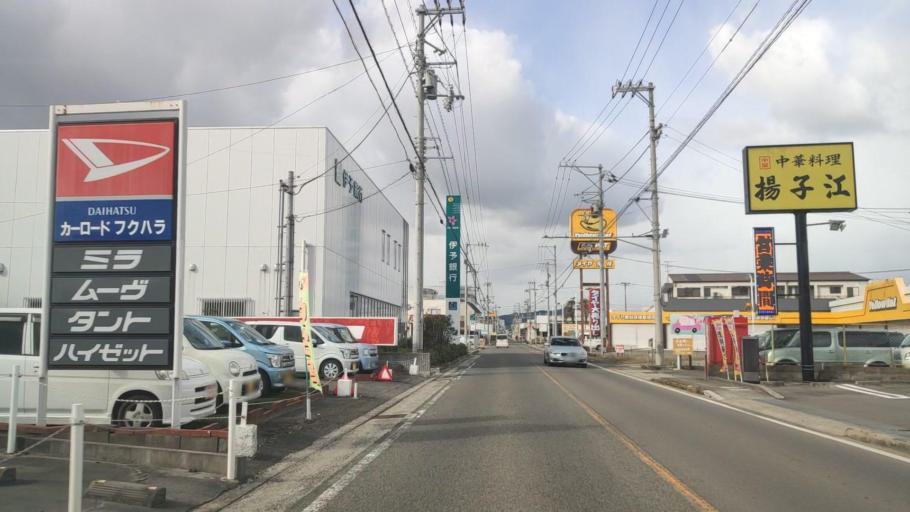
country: JP
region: Ehime
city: Saijo
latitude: 34.0503
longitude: 133.0141
